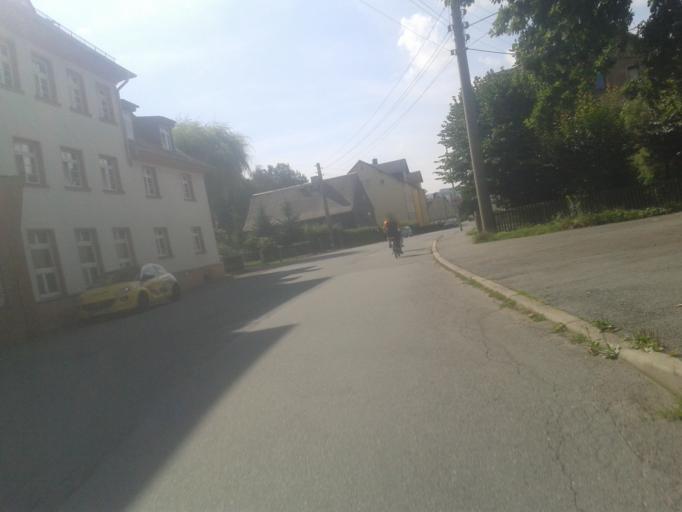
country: DE
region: Saxony
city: Neukirchen
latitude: 50.7754
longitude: 12.8789
